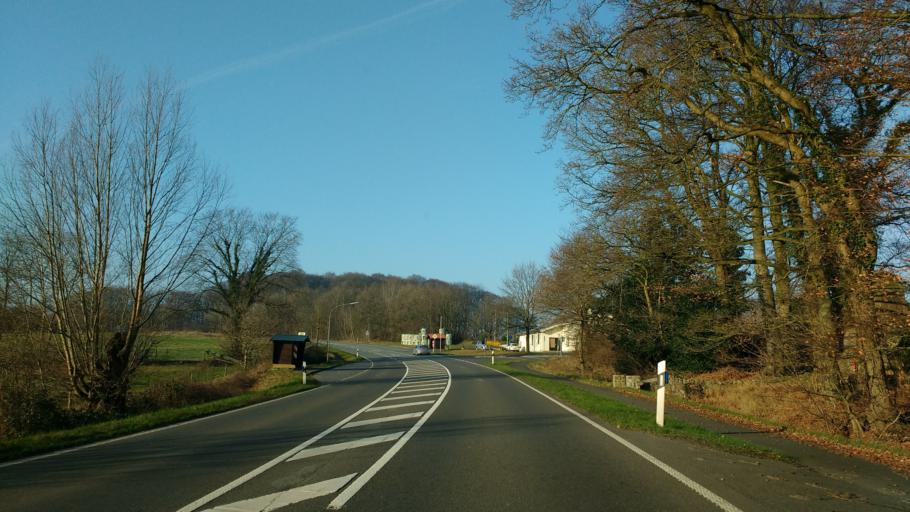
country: DE
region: Schleswig-Holstein
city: Nienbuttel
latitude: 54.0270
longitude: 9.4154
